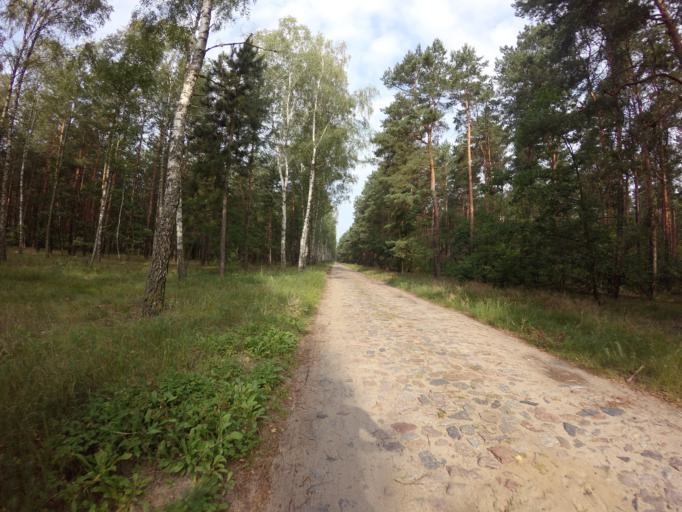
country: PL
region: Kujawsko-Pomorskie
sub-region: Bydgoszcz
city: Bydgoszcz
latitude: 53.1470
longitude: 18.0438
